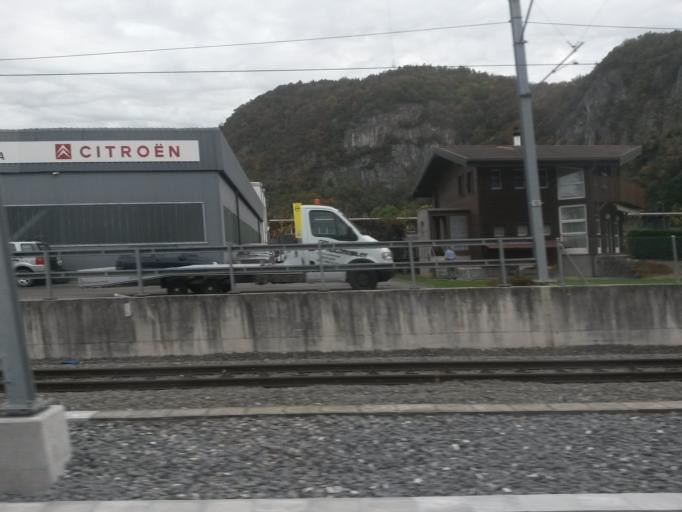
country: CH
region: Vaud
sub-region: Aigle District
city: Aigle
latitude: 46.3084
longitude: 6.9663
